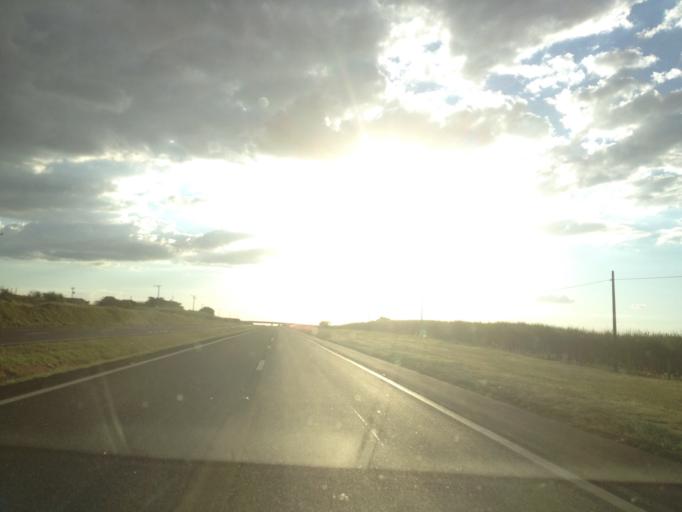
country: BR
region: Sao Paulo
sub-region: Jau
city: Jau
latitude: -22.2700
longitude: -48.4815
